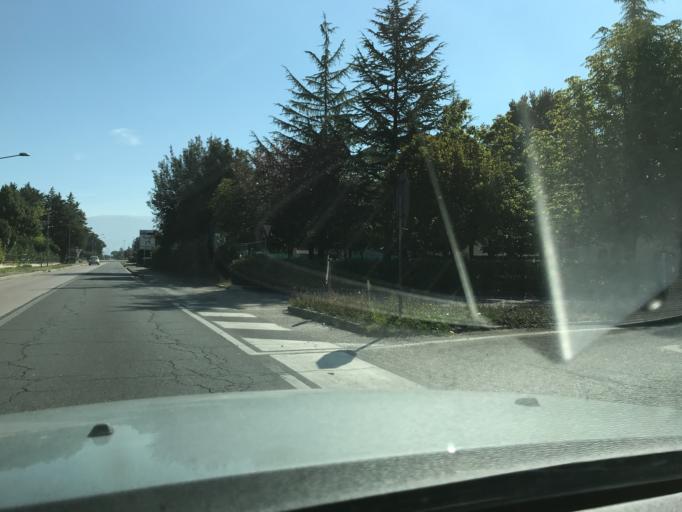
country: IT
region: Umbria
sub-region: Provincia di Perugia
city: Ospedalicchio
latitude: 43.0790
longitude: 12.5056
